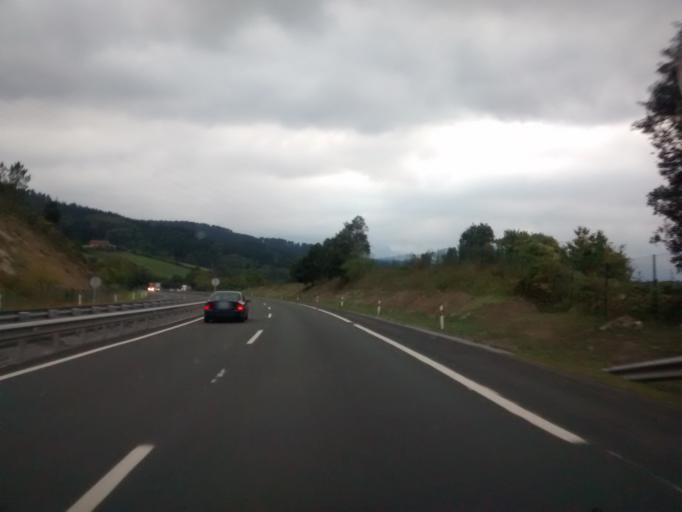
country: ES
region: Basque Country
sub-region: Bizkaia
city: Zaldibar
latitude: 43.1709
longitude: -2.5401
